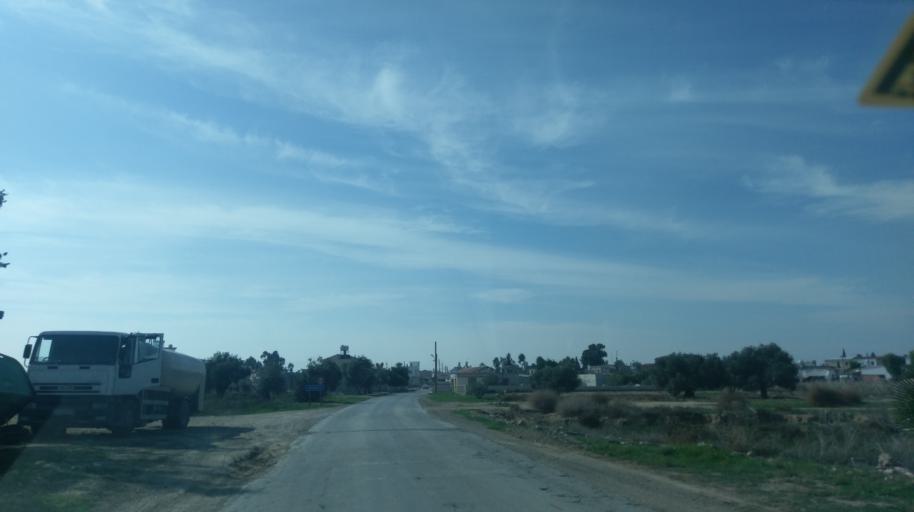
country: CY
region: Larnaka
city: Pergamos
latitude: 35.1378
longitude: 33.6606
